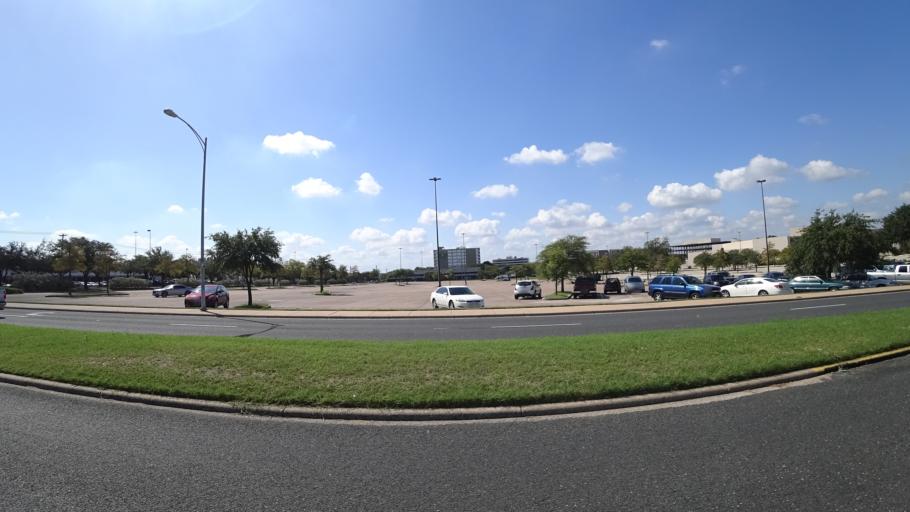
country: US
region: Texas
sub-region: Travis County
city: Austin
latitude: 30.3266
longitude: -97.7090
